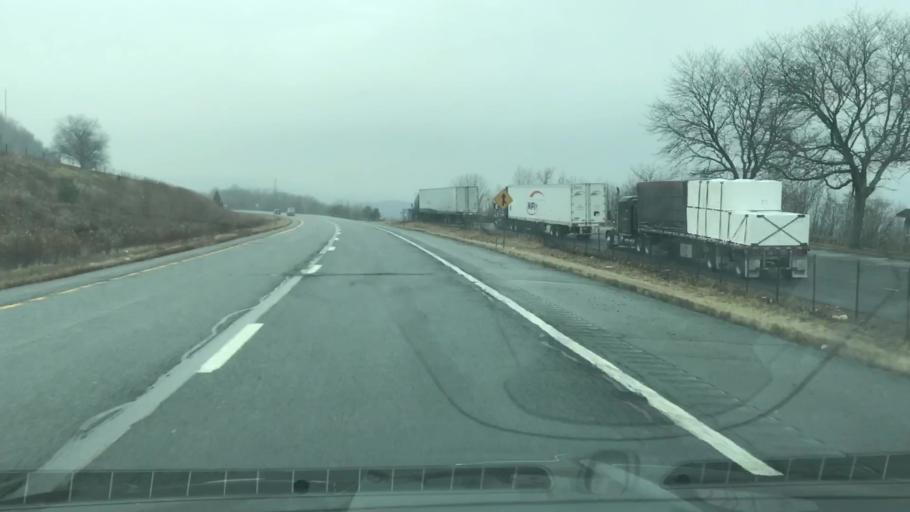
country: US
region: New York
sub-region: Orange County
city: Port Jervis
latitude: 41.3735
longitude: -74.6385
